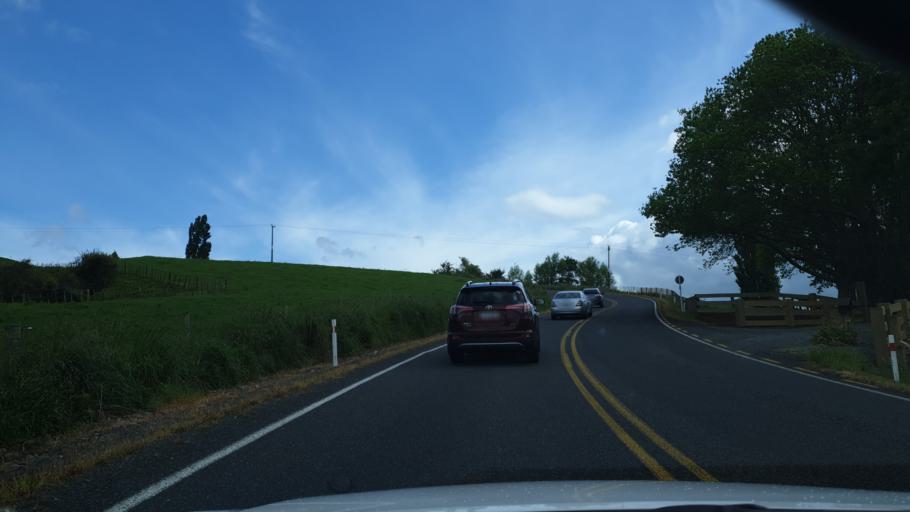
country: NZ
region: Waikato
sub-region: Matamata-Piako District
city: Matamata
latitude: -37.8804
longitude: 175.6929
